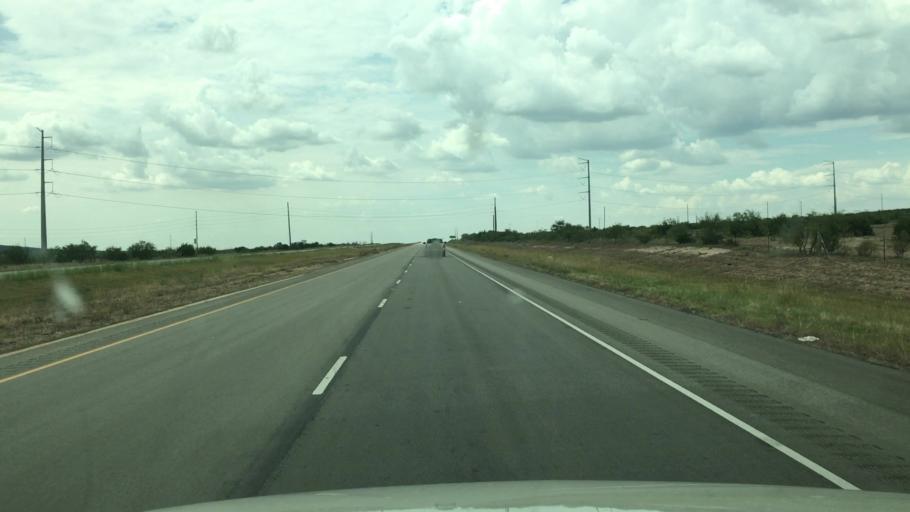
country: US
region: Texas
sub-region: Glasscock County
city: Garden City
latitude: 31.9863
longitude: -101.2623
